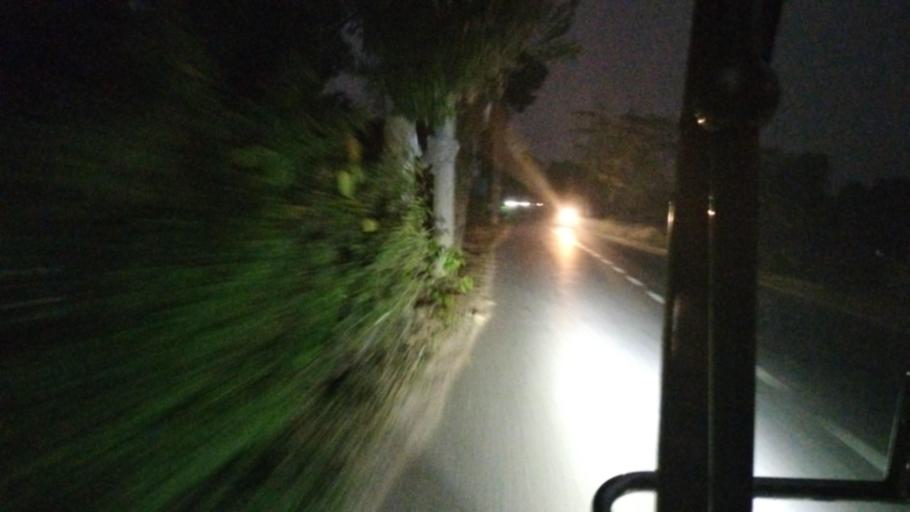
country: BD
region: Dhaka
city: Gafargaon
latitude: 24.4000
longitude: 90.3665
